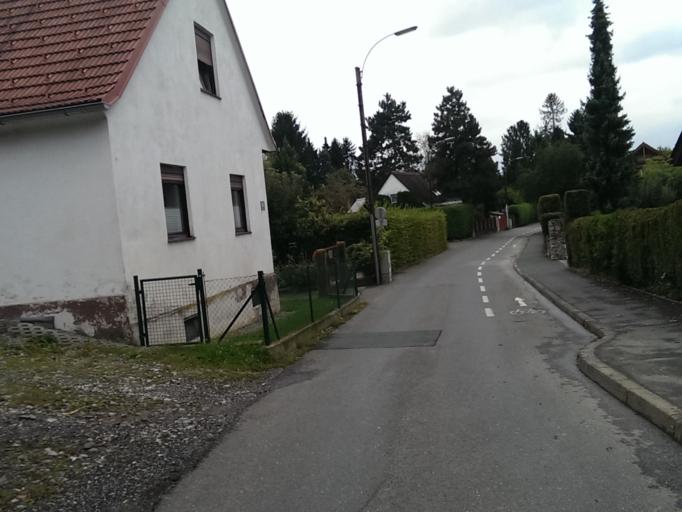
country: AT
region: Styria
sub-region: Graz Stadt
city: Graz
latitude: 47.0542
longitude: 15.4766
